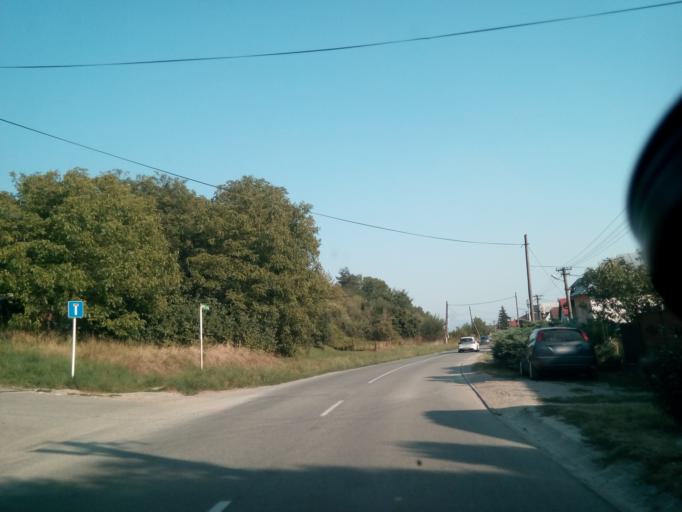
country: SK
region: Kosicky
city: Kosice
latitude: 48.7140
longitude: 21.1973
